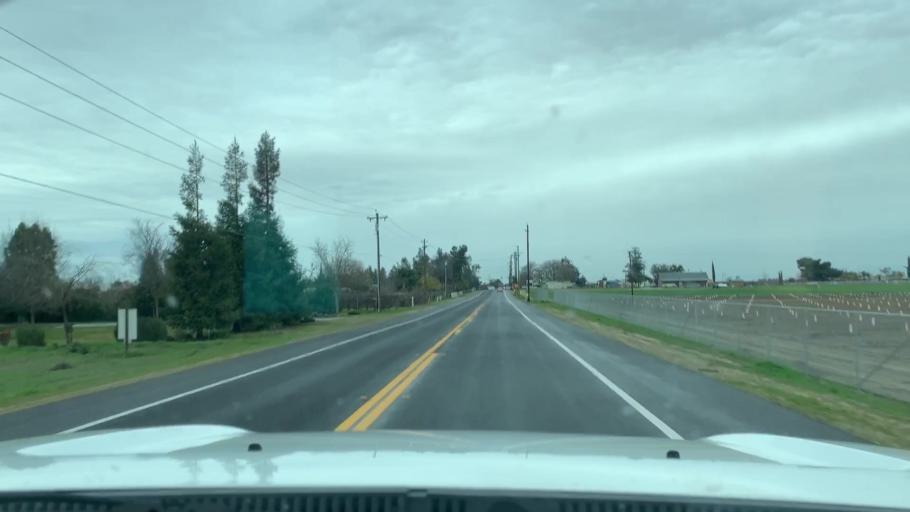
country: US
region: California
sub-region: Fresno County
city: Fowler
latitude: 36.5728
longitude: -119.6825
